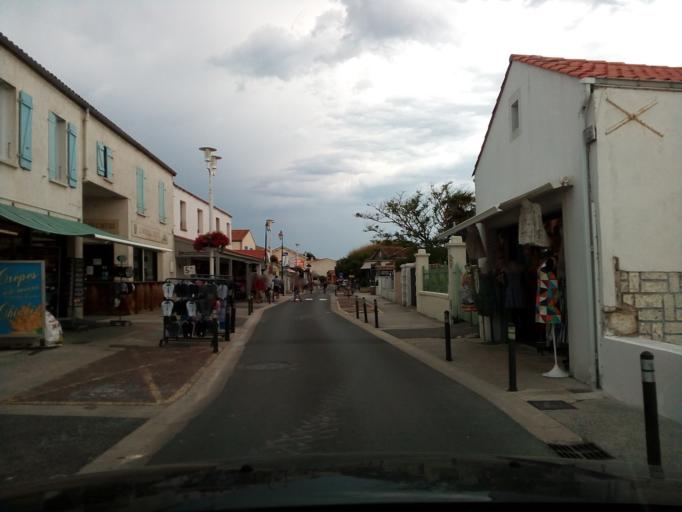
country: FR
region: Poitou-Charentes
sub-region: Departement de la Charente-Maritime
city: Dolus-d'Oleron
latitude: 45.9163
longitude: -1.3291
